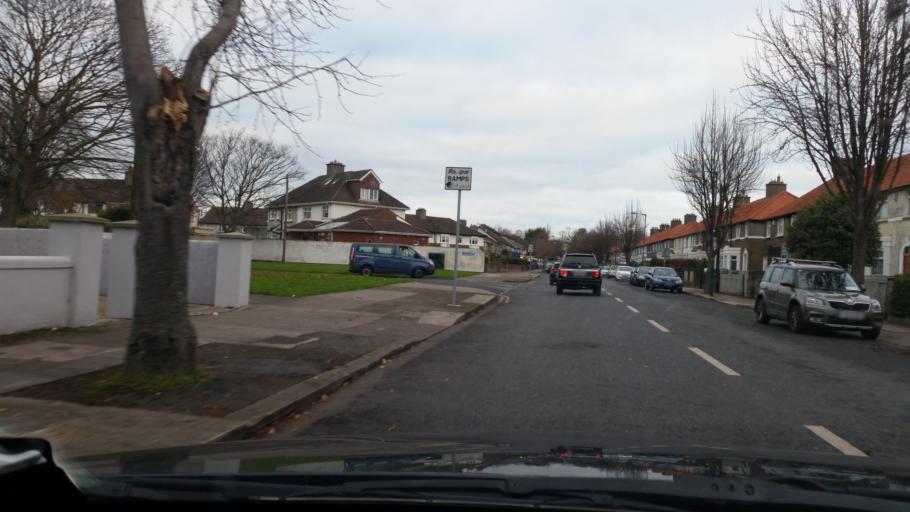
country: IE
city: Fairview
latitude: 53.3689
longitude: -6.2393
